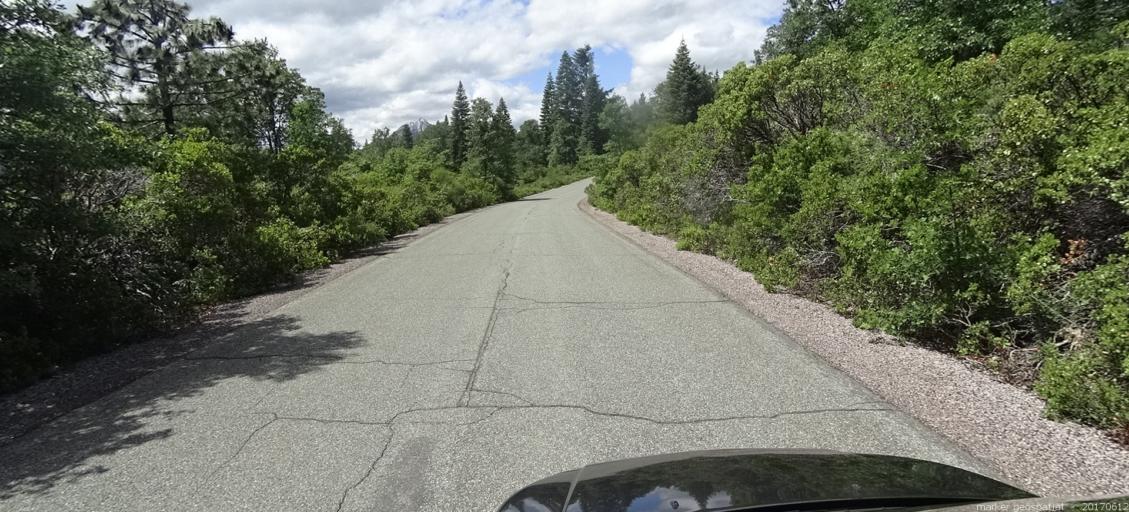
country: US
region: California
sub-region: Siskiyou County
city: Mount Shasta
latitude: 41.3016
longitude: -122.2895
